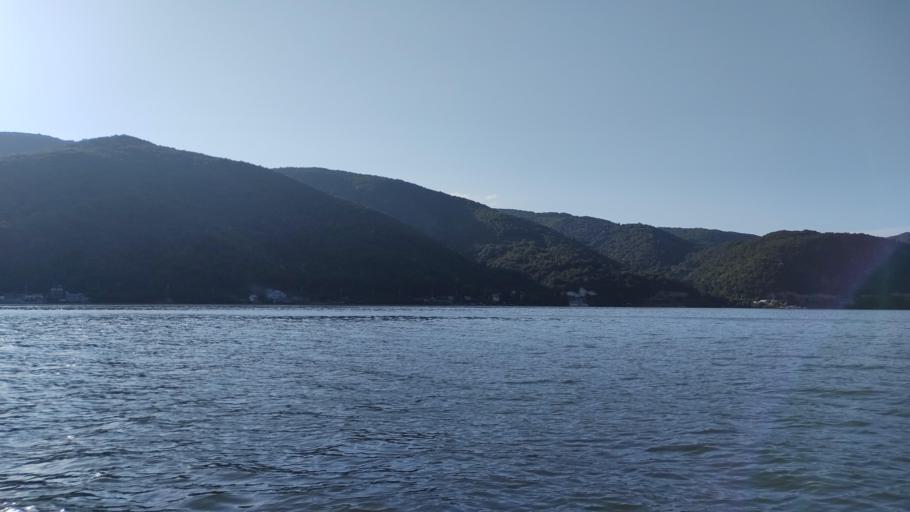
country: RO
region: Mehedinti
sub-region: Comuna Dubova
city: Dubova
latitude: 44.5718
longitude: 22.2418
